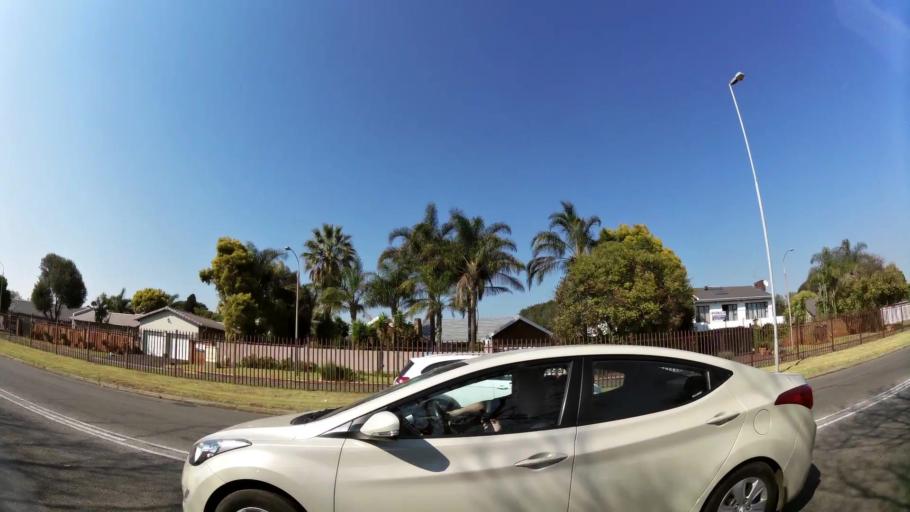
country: ZA
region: Gauteng
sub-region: Ekurhuleni Metropolitan Municipality
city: Boksburg
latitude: -26.2441
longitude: 28.2602
